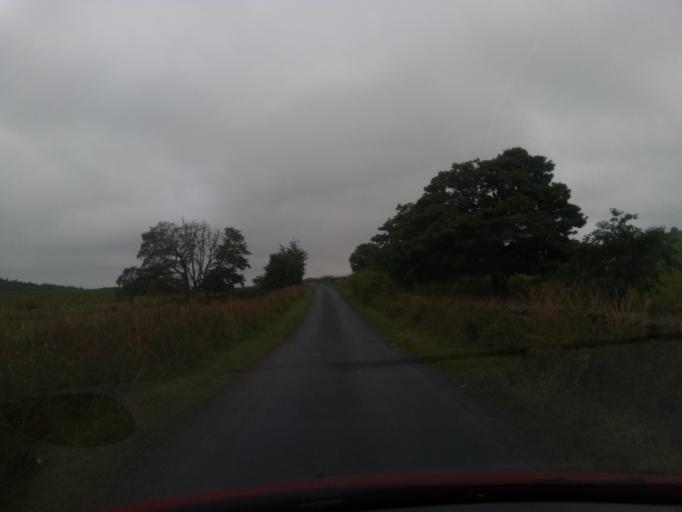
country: GB
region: Scotland
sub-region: The Scottish Borders
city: Galashiels
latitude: 55.6793
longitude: -2.8765
